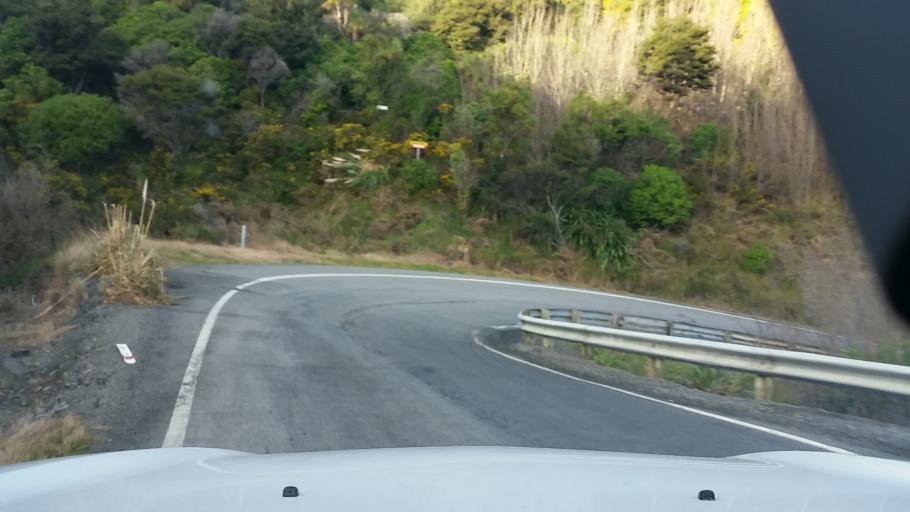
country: NZ
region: Wellington
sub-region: South Wairarapa District
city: Waipawa
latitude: -41.4555
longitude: 175.2220
